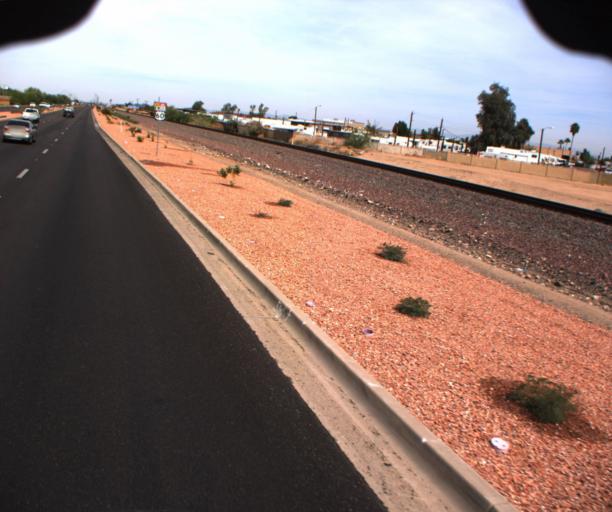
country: US
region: Arizona
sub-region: Maricopa County
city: Peoria
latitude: 33.5678
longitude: -112.2213
